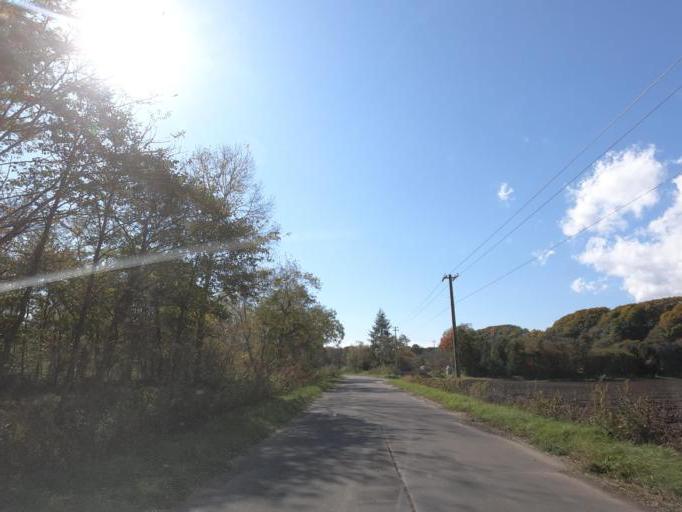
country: JP
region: Hokkaido
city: Otofuke
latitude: 43.2352
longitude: 143.2663
